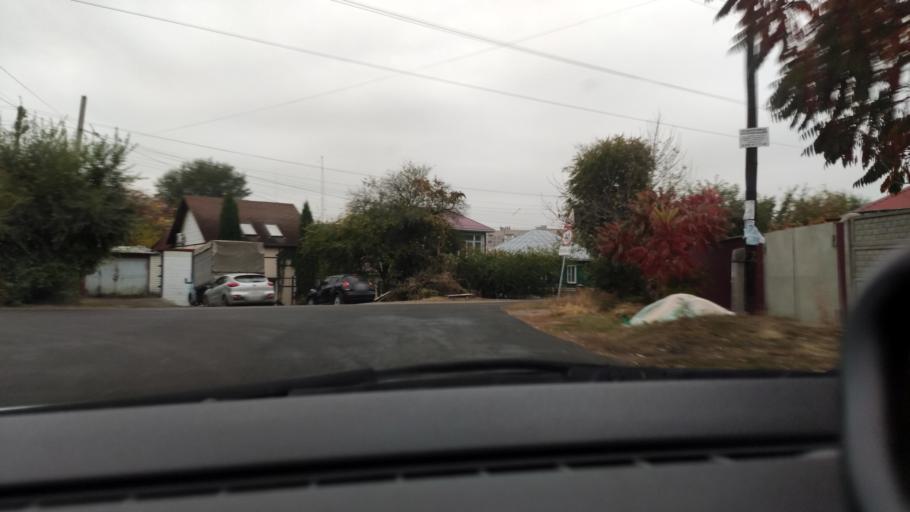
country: RU
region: Voronezj
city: Voronezh
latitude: 51.6900
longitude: 39.2043
